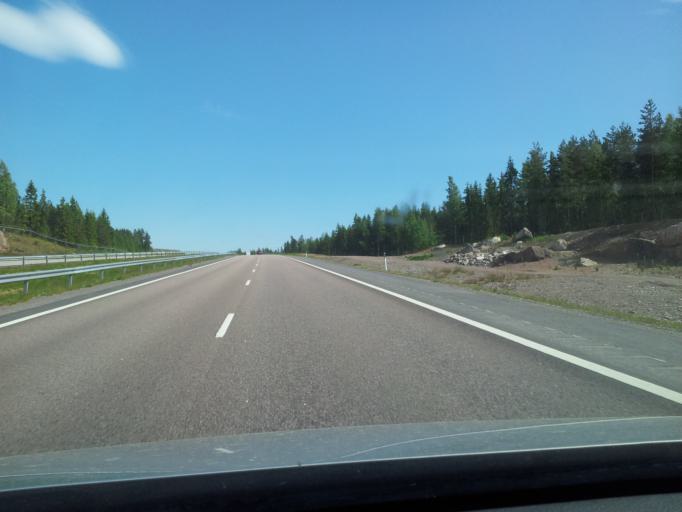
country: FI
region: Uusimaa
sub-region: Loviisa
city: Perna
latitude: 60.4847
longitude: 26.0180
